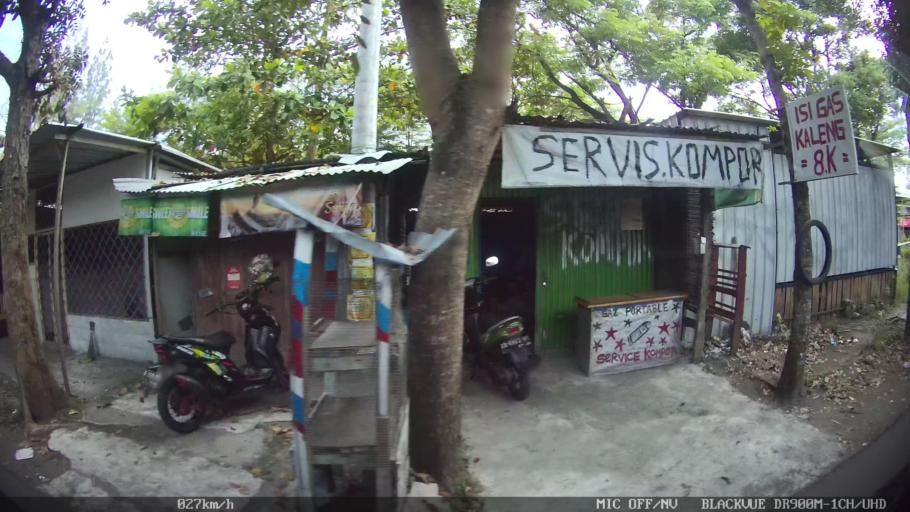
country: ID
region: Daerah Istimewa Yogyakarta
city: Depok
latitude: -7.7463
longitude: 110.4179
